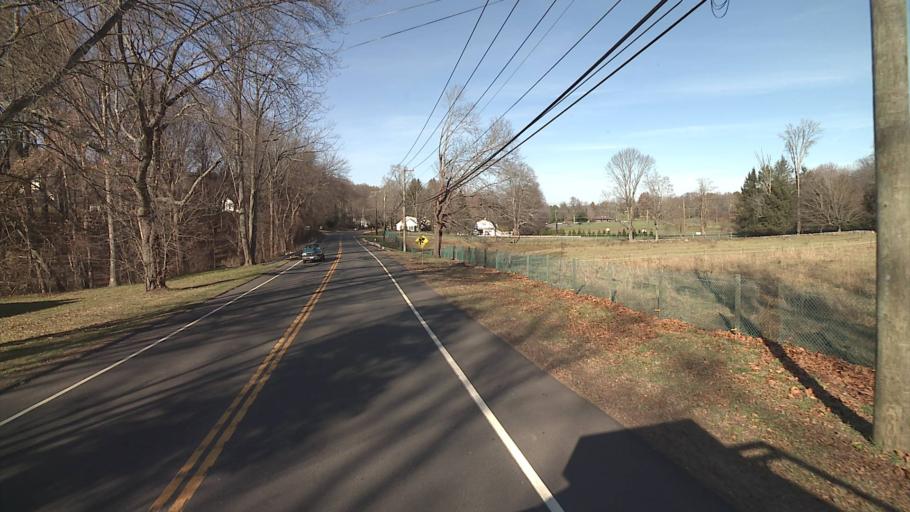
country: US
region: Connecticut
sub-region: Middlesex County
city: Portland
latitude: 41.5794
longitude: -72.6082
